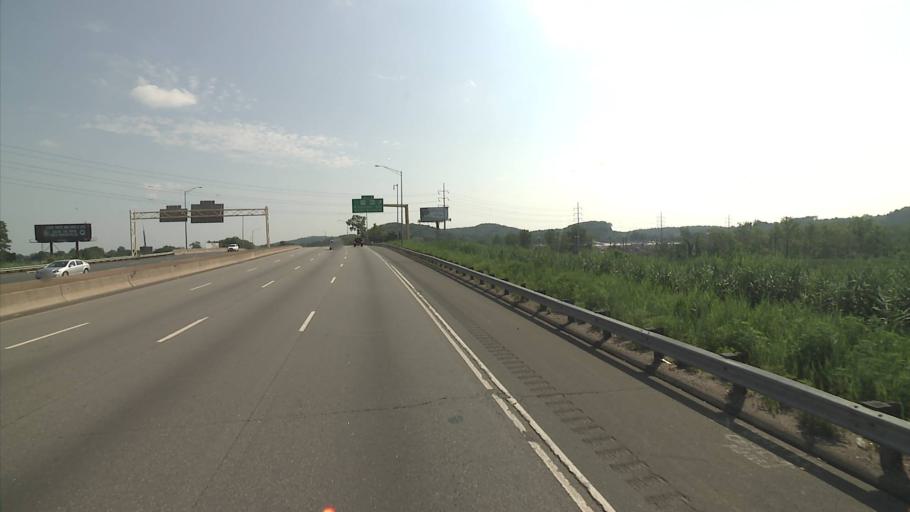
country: US
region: Connecticut
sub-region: New Haven County
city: New Haven
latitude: 41.3216
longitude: -72.8866
